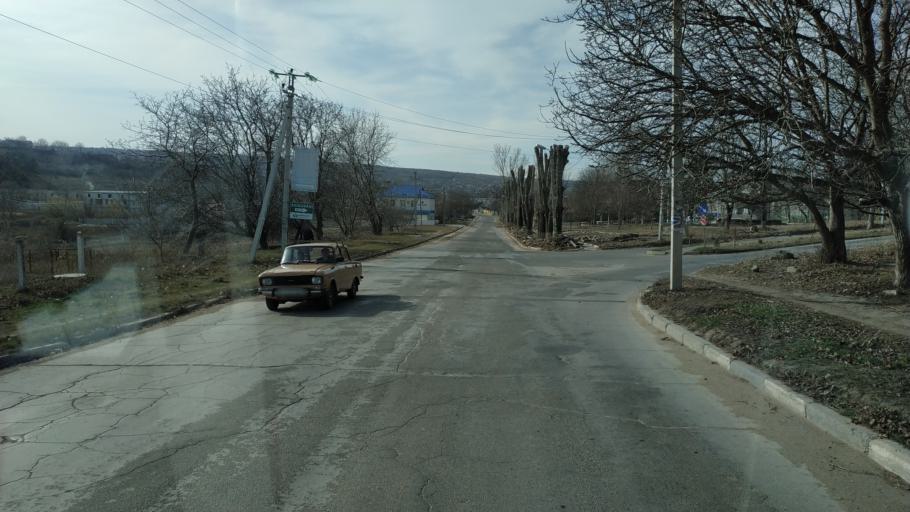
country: MD
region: Chisinau
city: Vatra
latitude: 47.0724
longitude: 28.6953
